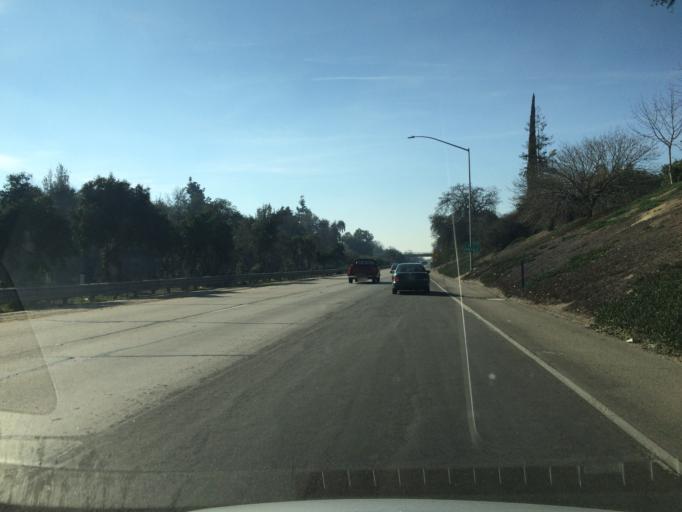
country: US
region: California
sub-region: Tulare County
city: Visalia
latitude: 36.3271
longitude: -119.3011
